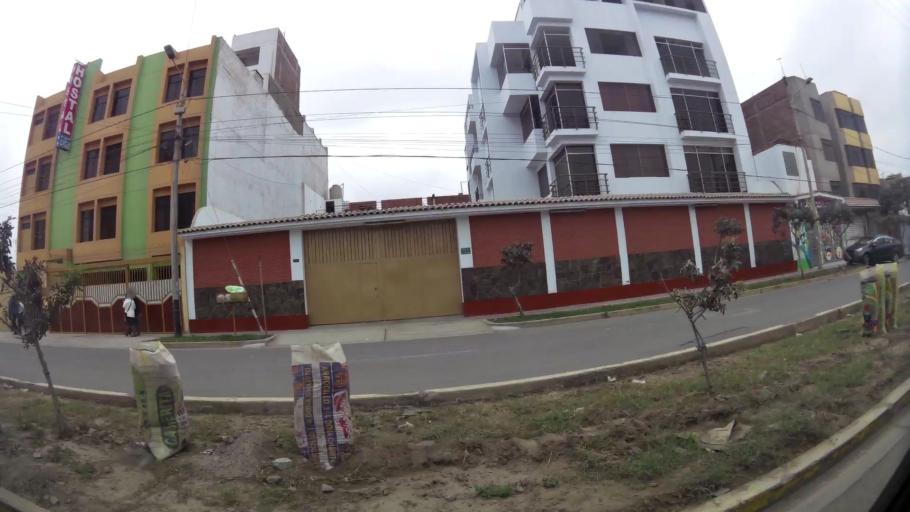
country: PE
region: La Libertad
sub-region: Provincia de Trujillo
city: Buenos Aires
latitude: -8.1231
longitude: -79.0455
